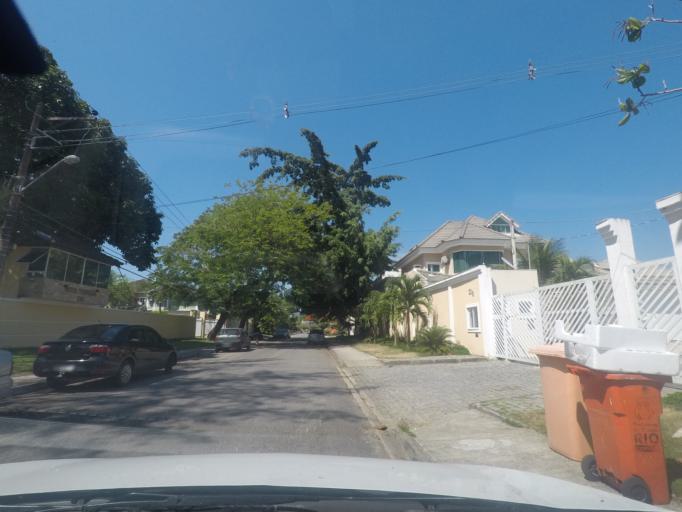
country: BR
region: Rio de Janeiro
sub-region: Nilopolis
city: Nilopolis
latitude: -22.9840
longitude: -43.4547
